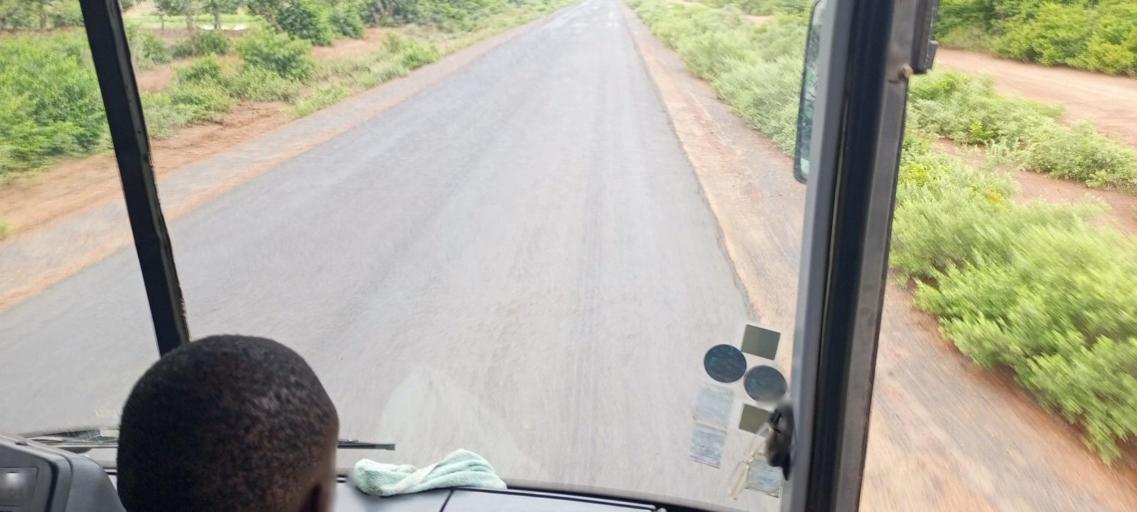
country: ML
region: Sikasso
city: Koutiala
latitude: 12.5731
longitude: -5.6042
